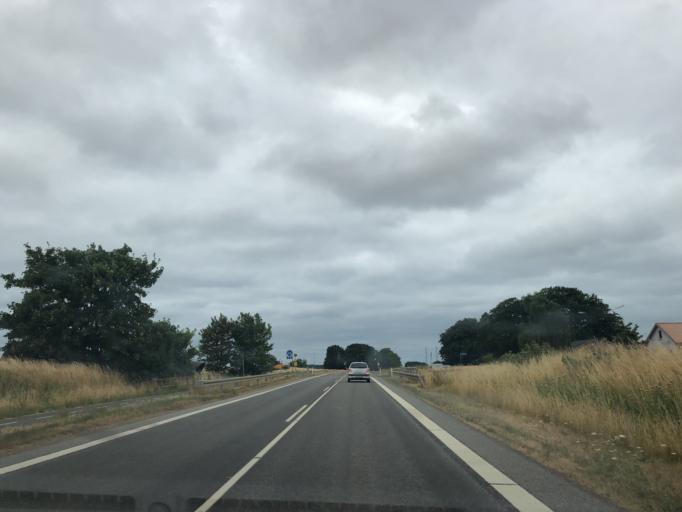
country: DK
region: Zealand
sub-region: Slagelse Kommune
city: Skaelskor
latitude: 55.2220
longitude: 11.3049
